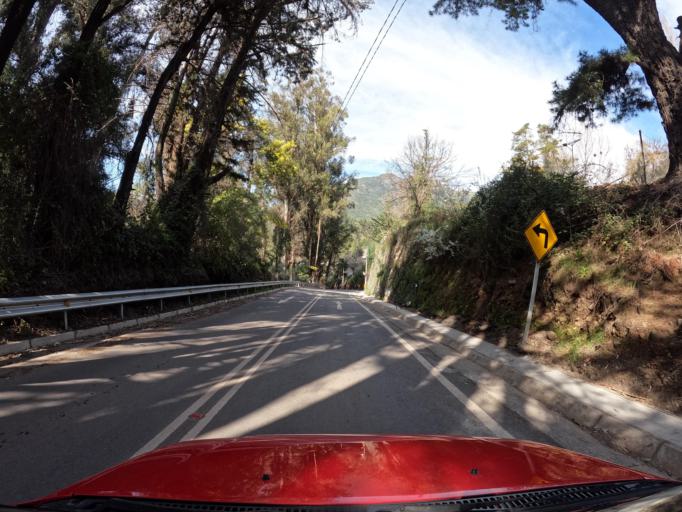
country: CL
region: O'Higgins
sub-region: Provincia de Colchagua
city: Chimbarongo
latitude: -35.0010
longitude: -70.8142
